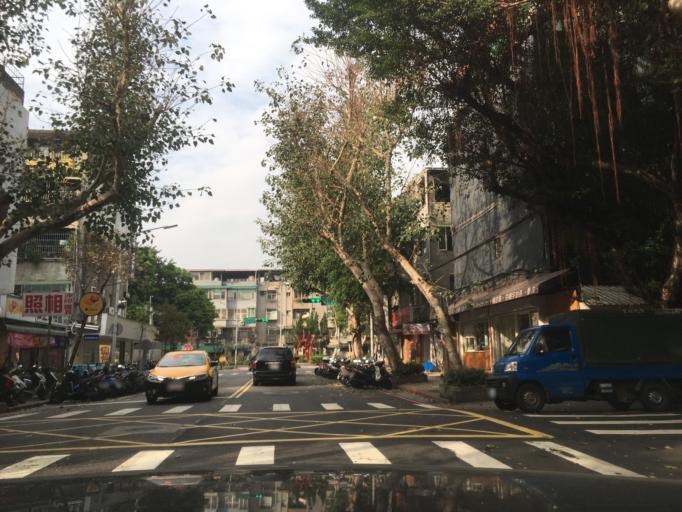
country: TW
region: Taipei
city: Taipei
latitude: 25.0575
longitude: 121.5530
